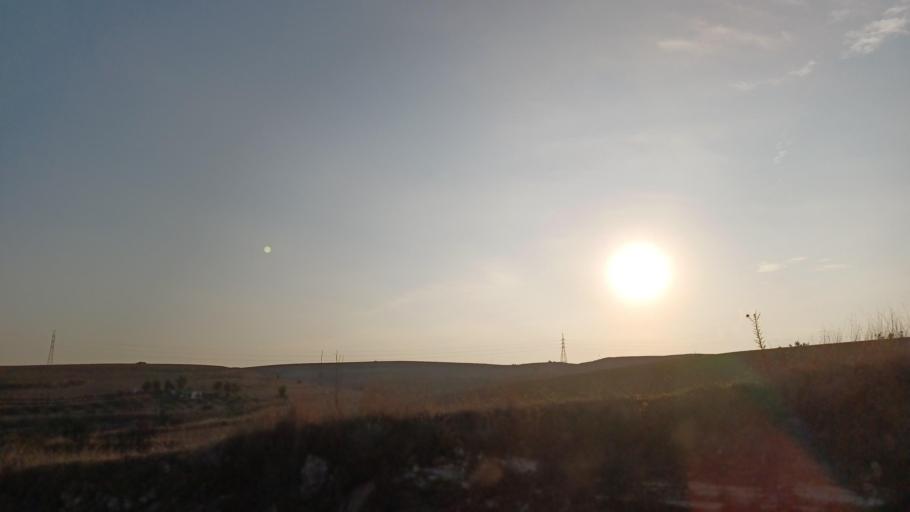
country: CY
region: Larnaka
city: Athienou
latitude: 35.0245
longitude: 33.5540
